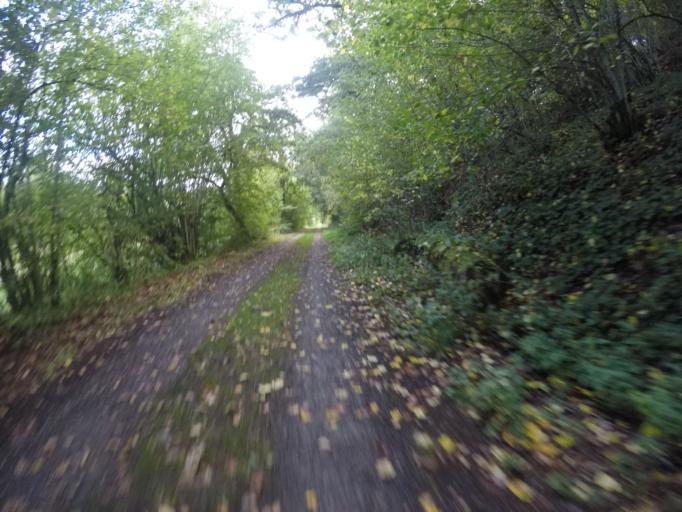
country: BE
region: Wallonia
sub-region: Province du Luxembourg
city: Fauvillers
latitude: 49.9133
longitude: 5.6891
